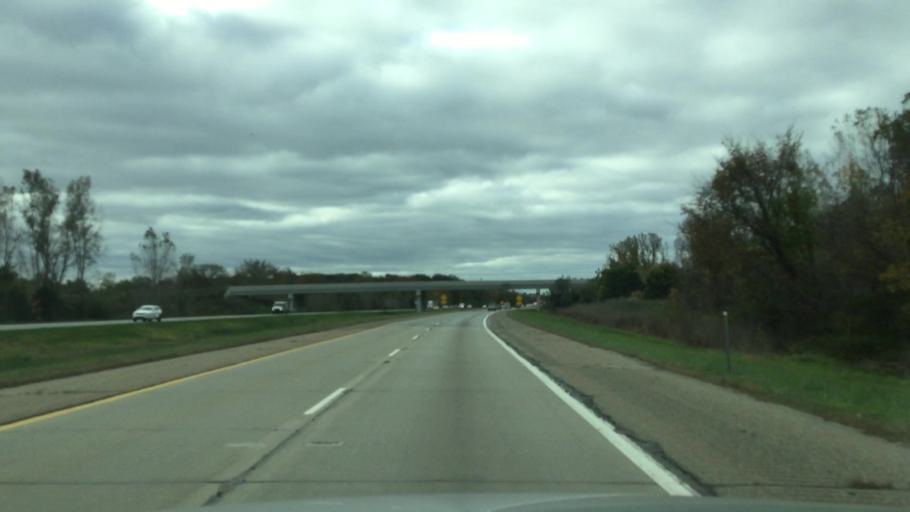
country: US
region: Michigan
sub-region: Macomb County
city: Romeo
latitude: 42.7456
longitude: -83.0212
